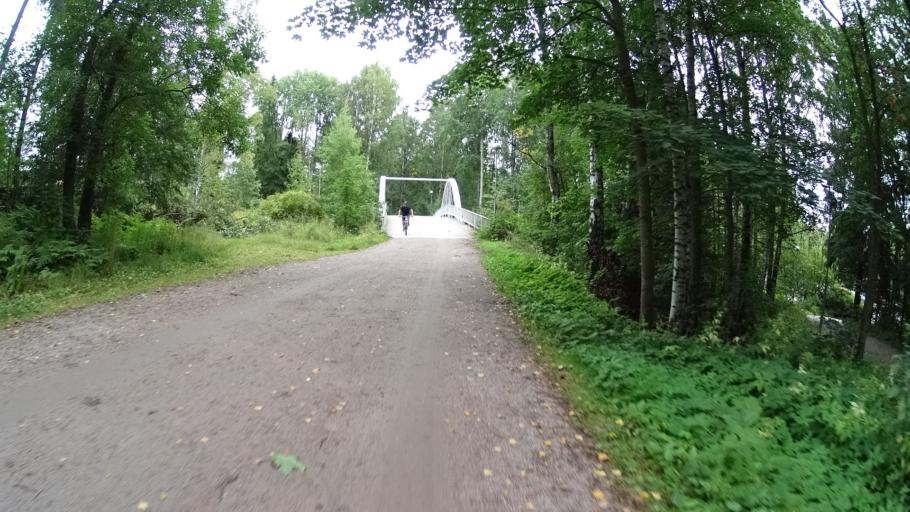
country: FI
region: Uusimaa
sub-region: Helsinki
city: Helsinki
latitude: 60.2307
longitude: 24.9143
